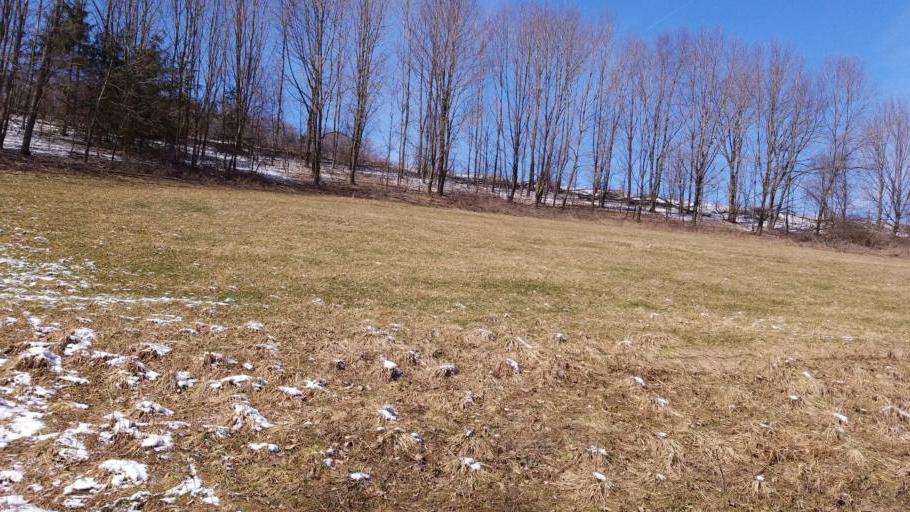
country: US
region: Pennsylvania
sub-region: Tioga County
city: Westfield
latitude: 41.9467
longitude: -77.7285
